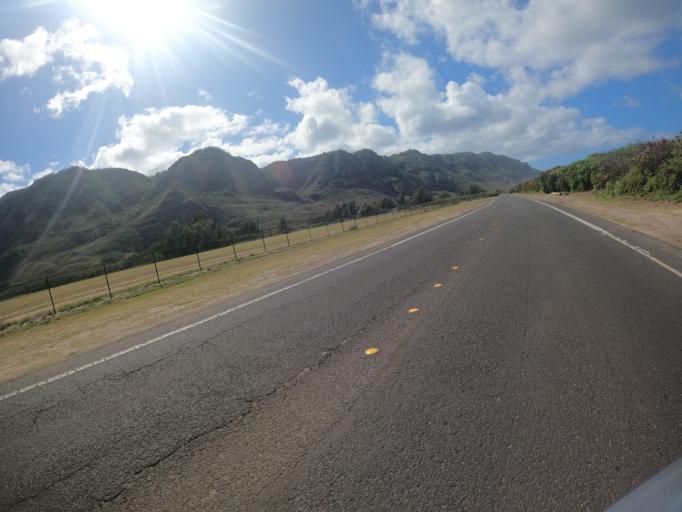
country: US
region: Hawaii
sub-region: Honolulu County
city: Mokuleia
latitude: 21.5813
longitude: -158.2112
